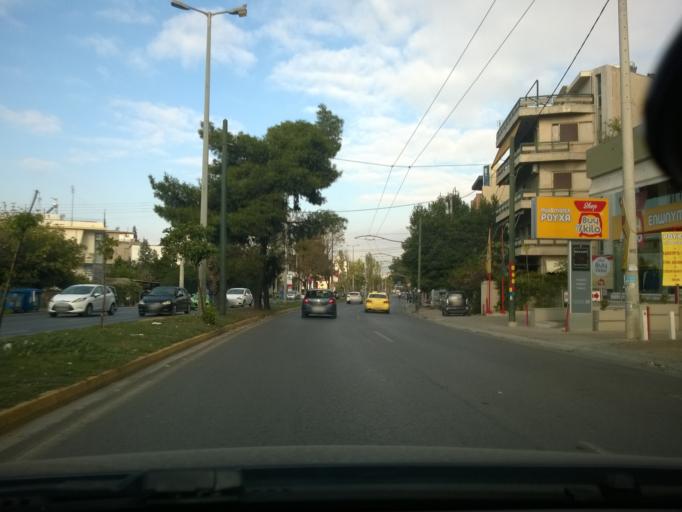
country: GR
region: Attica
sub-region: Nomarchia Athinas
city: Khalandrion
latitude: 38.0184
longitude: 23.7954
